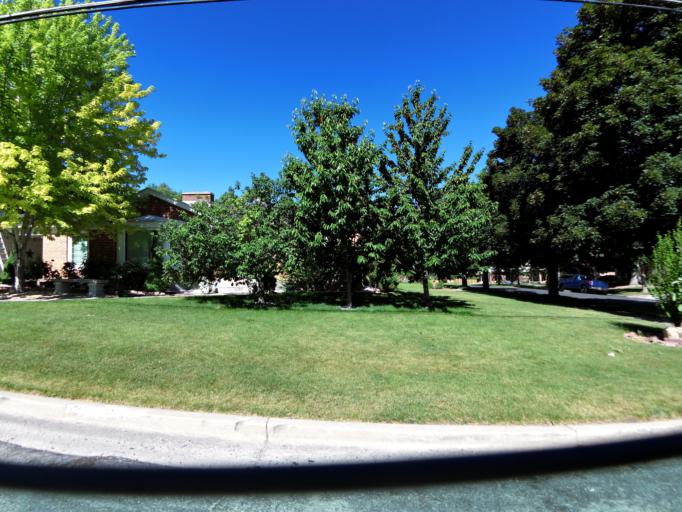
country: US
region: Utah
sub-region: Weber County
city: Ogden
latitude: 41.2150
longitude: -111.9456
